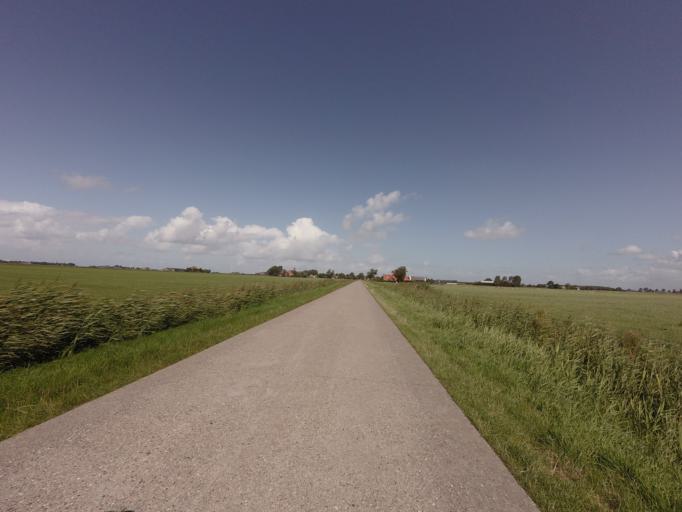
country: NL
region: Friesland
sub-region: Sudwest Fryslan
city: Makkum
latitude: 53.0736
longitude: 5.4535
